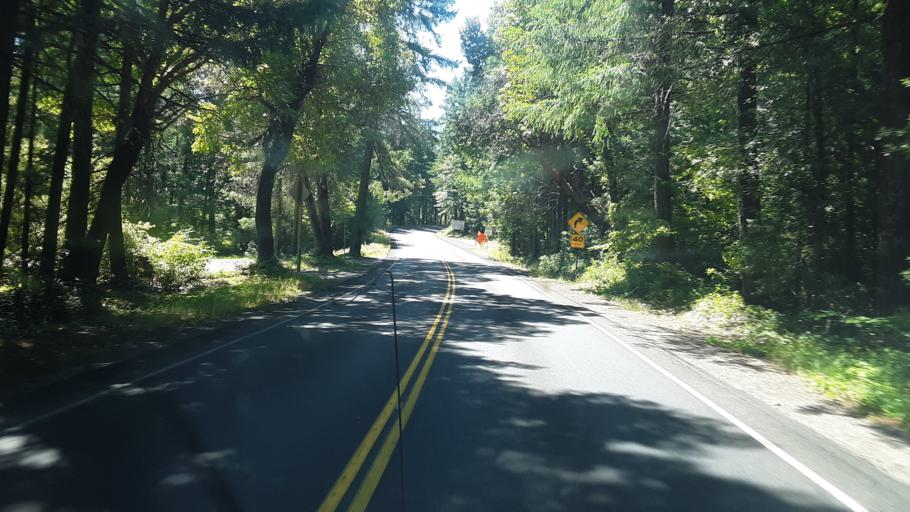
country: US
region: Oregon
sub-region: Josephine County
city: Cave Junction
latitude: 41.9927
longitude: -123.7194
